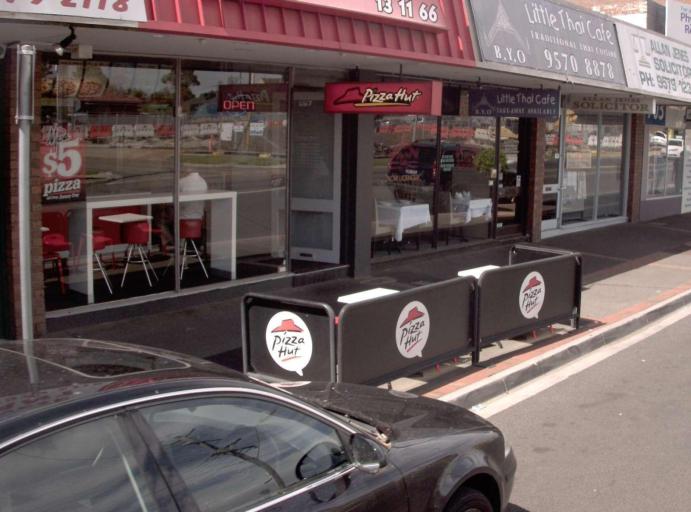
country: AU
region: Victoria
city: McKinnon
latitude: -37.9206
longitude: 145.0549
